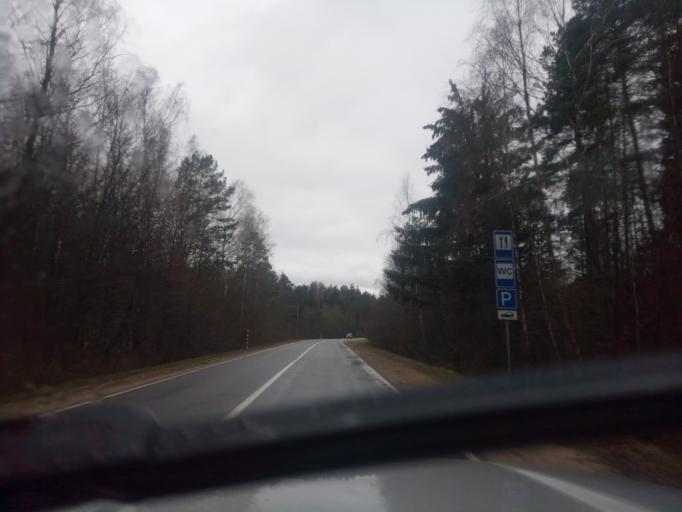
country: BY
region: Minsk
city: Kapyl'
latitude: 53.1614
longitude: 27.1154
